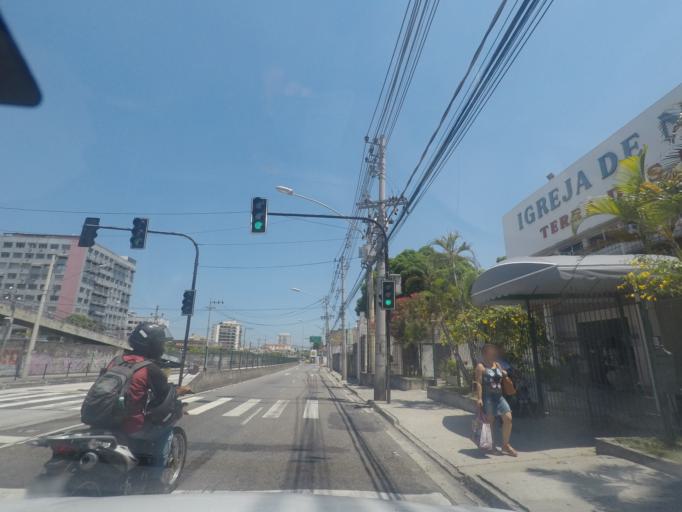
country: BR
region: Rio de Janeiro
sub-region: Duque De Caxias
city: Duque de Caxias
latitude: -22.8443
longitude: -43.2691
